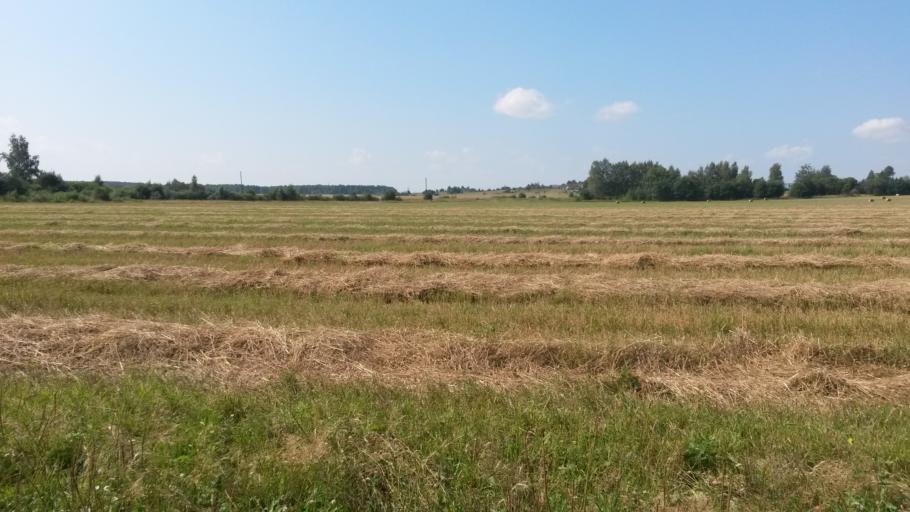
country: RU
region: Jaroslavl
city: Gavrilov-Yam
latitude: 57.3104
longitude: 39.9657
